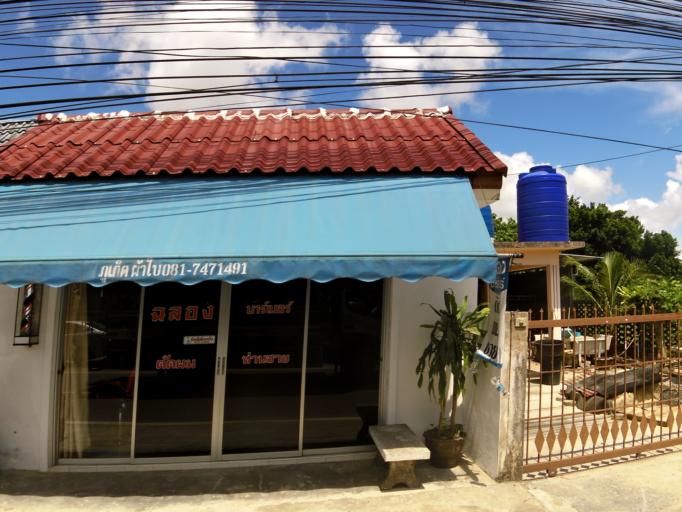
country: TH
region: Phuket
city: Ban Chalong
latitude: 7.8370
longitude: 98.3364
